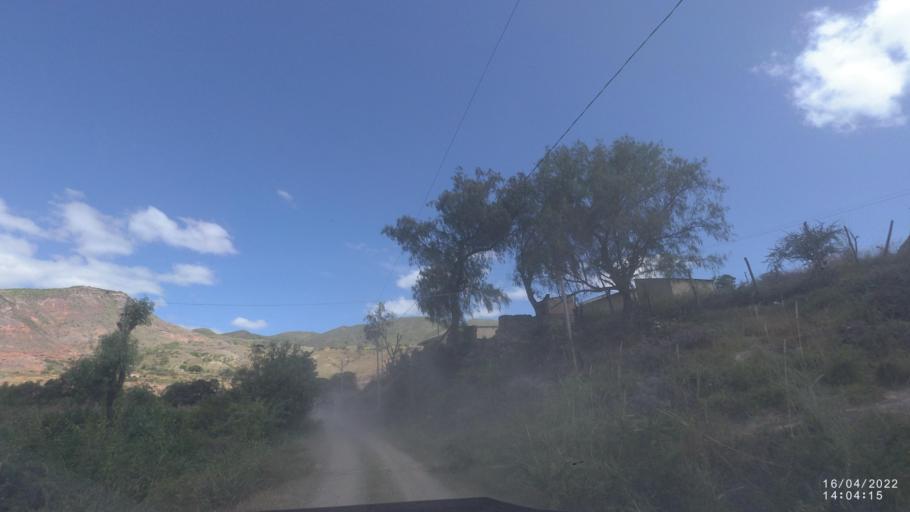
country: BO
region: Cochabamba
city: Mizque
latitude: -18.0546
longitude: -65.5409
